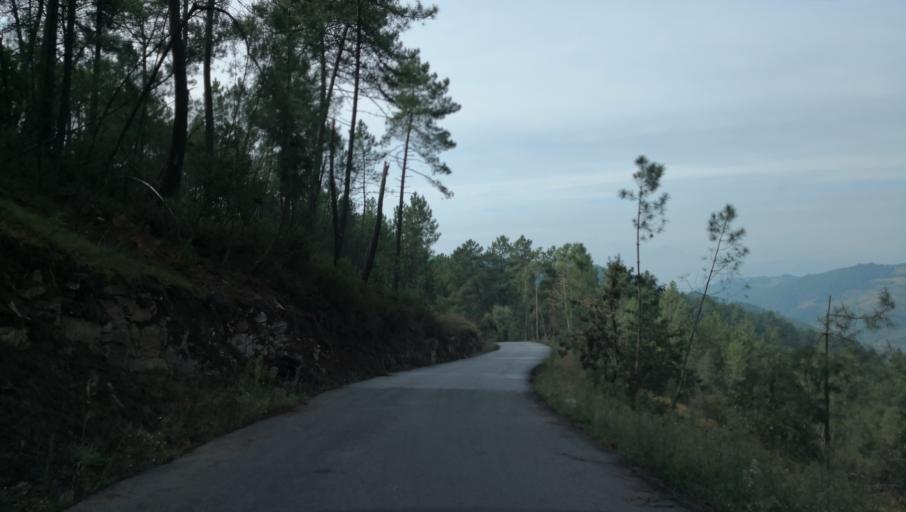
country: PT
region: Vila Real
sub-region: Sabrosa
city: Vilela
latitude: 41.2292
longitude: -7.6805
